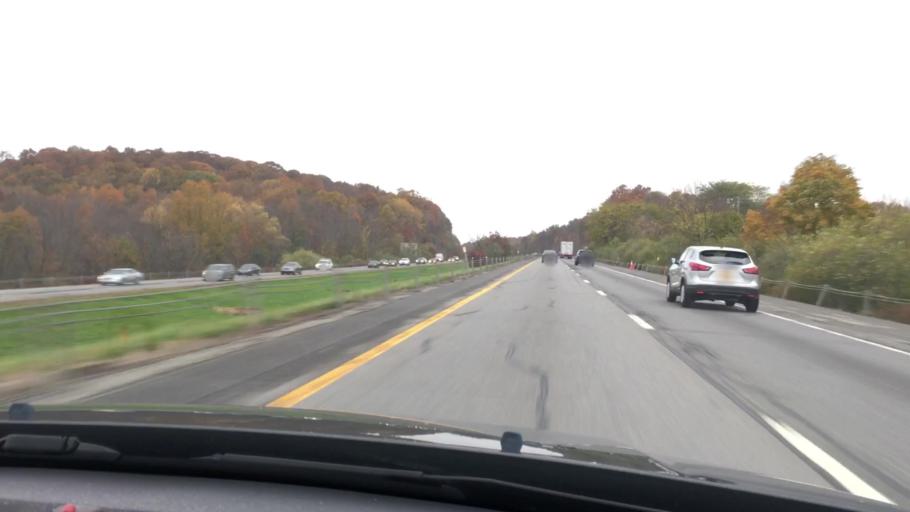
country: US
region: New York
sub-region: Putnam County
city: Brewster Hill
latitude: 41.4342
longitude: -73.6309
